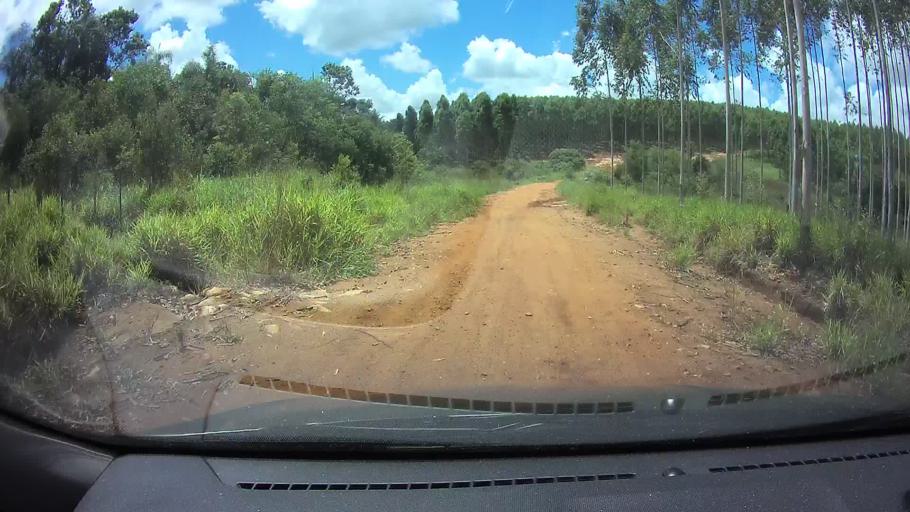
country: PY
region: Paraguari
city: La Colmena
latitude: -25.9649
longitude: -56.7415
